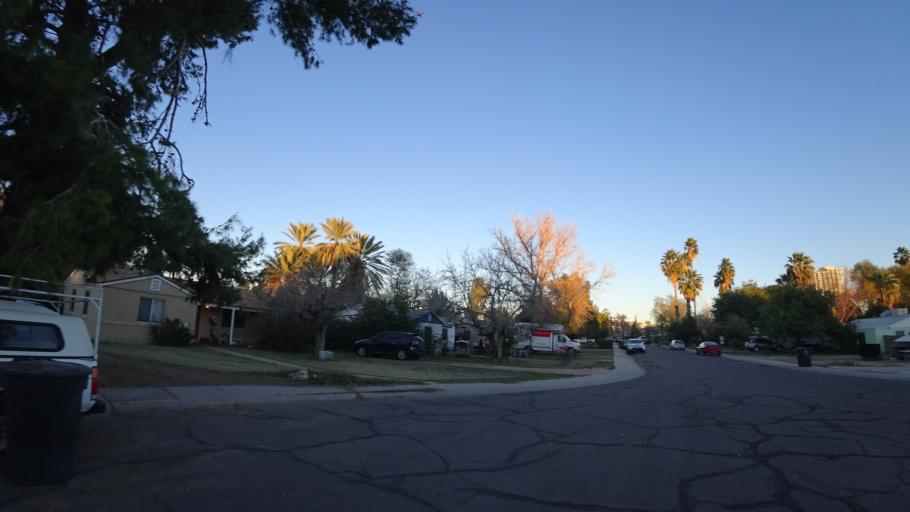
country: US
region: Arizona
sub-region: Maricopa County
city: Tempe Junction
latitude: 33.4272
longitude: -111.9491
